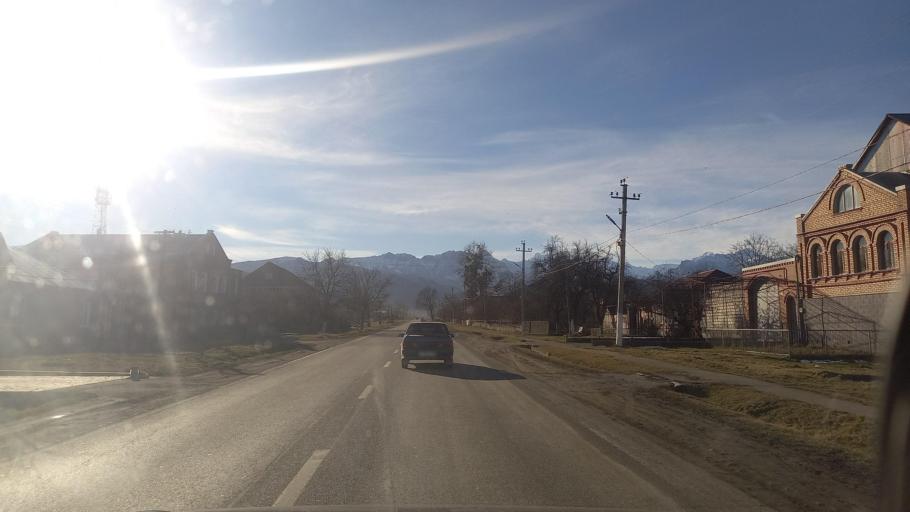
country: RU
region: North Ossetia
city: Gizel'
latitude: 43.0237
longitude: 44.5688
